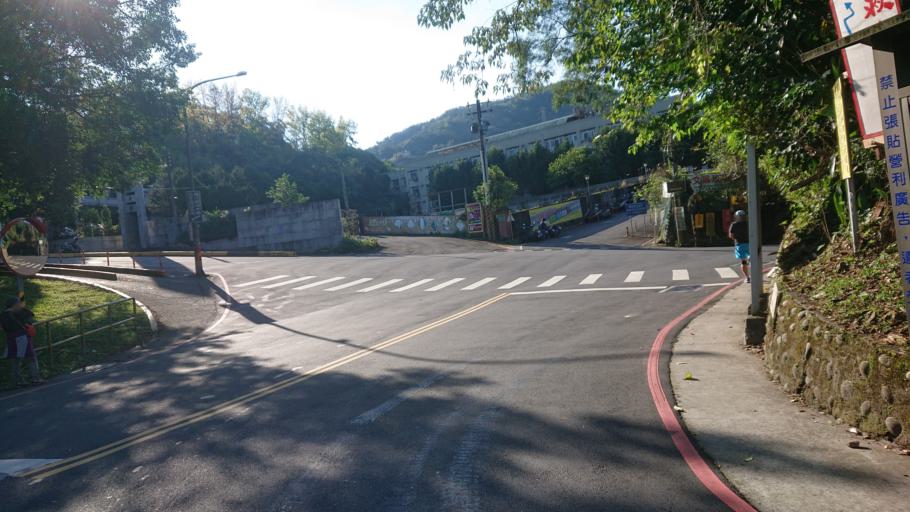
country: TW
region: Taipei
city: Taipei
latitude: 24.9799
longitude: 121.5677
